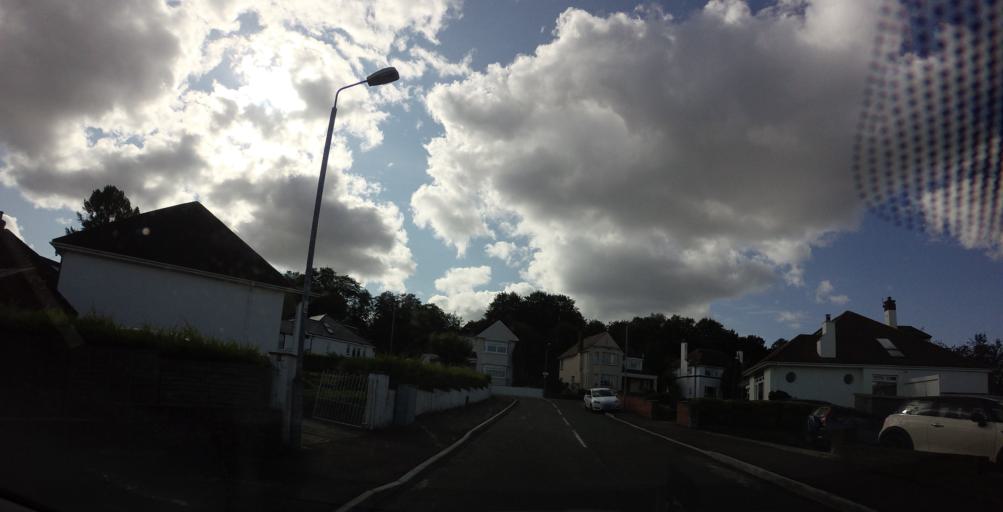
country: GB
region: Scotland
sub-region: North Lanarkshire
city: Coatbridge
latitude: 55.8608
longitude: -4.0500
